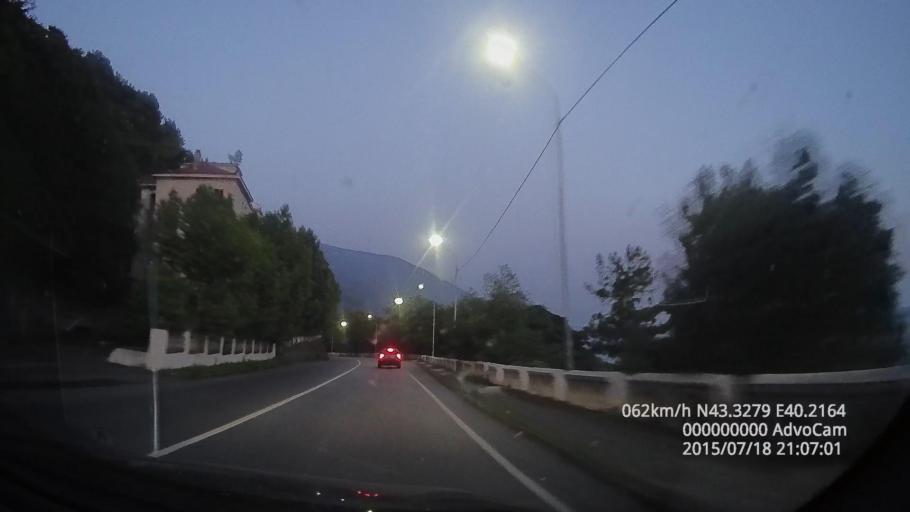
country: GE
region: Abkhazia
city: Gagra
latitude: 43.3277
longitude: 40.2168
